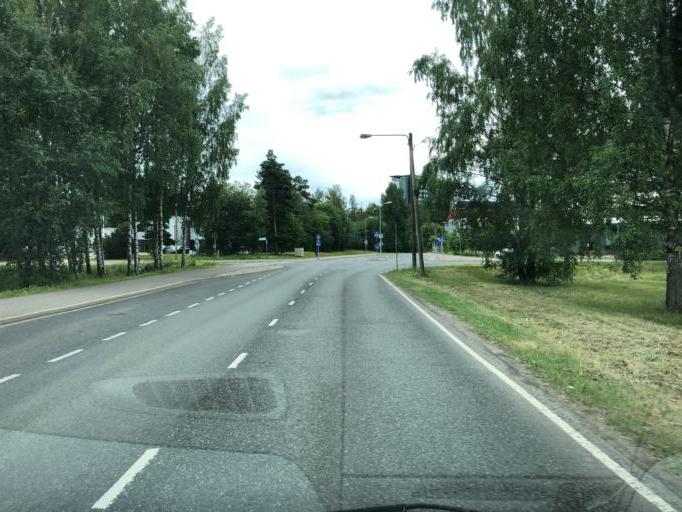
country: FI
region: Uusimaa
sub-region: Helsinki
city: Vantaa
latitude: 60.2944
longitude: 24.9720
